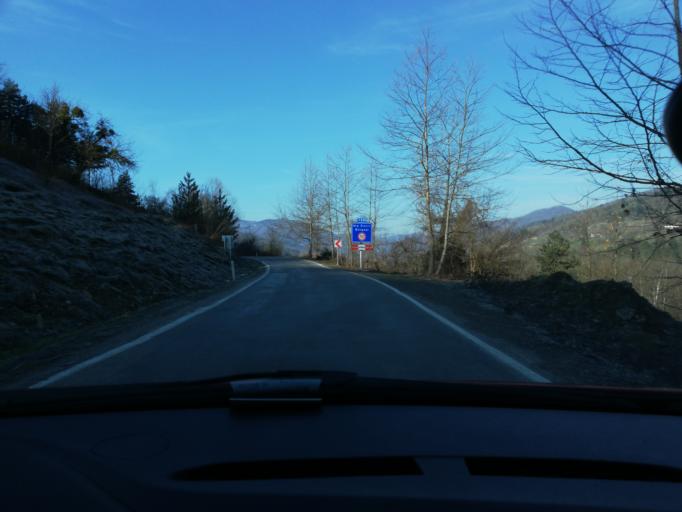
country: TR
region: Bartin
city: Kumluca
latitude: 41.4550
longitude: 32.5032
